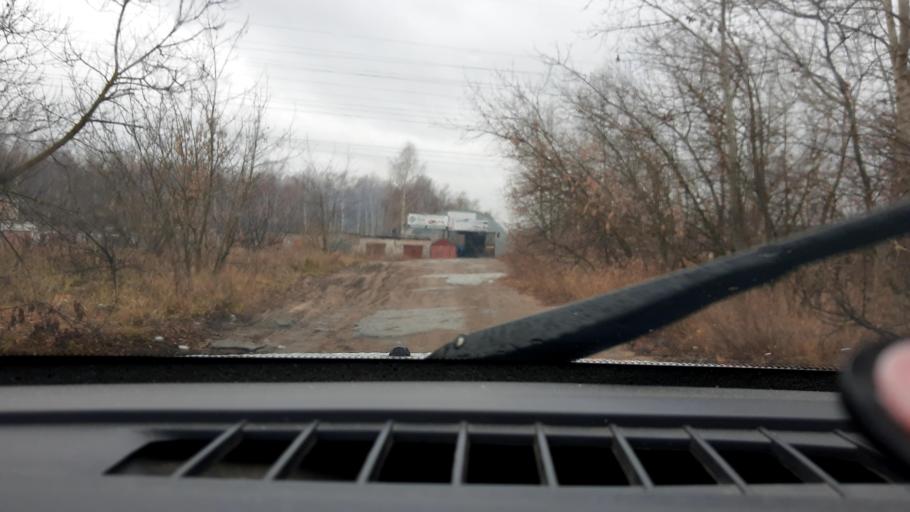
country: RU
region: Nizjnij Novgorod
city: Gorbatovka
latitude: 56.3523
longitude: 43.8279
